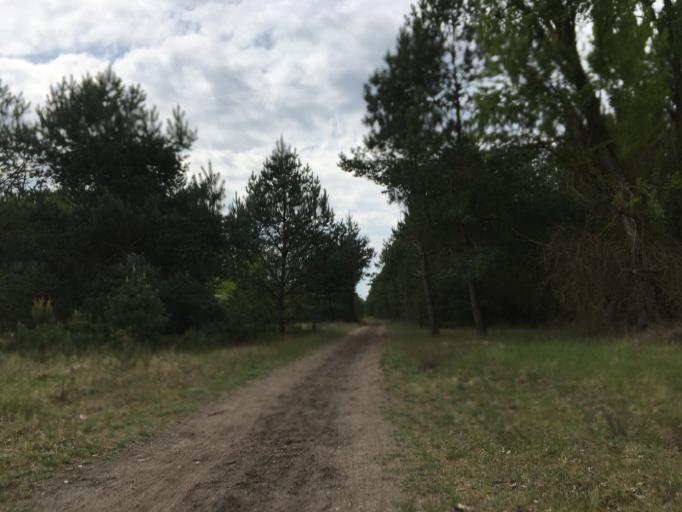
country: DE
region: Brandenburg
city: Rudnitz
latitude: 52.6973
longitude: 13.6143
